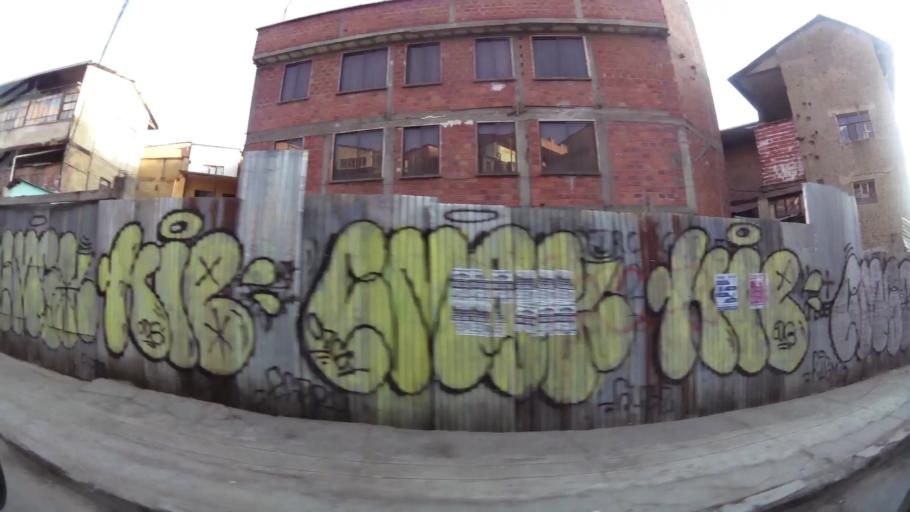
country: BO
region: La Paz
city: La Paz
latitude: -16.5007
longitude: -68.1357
